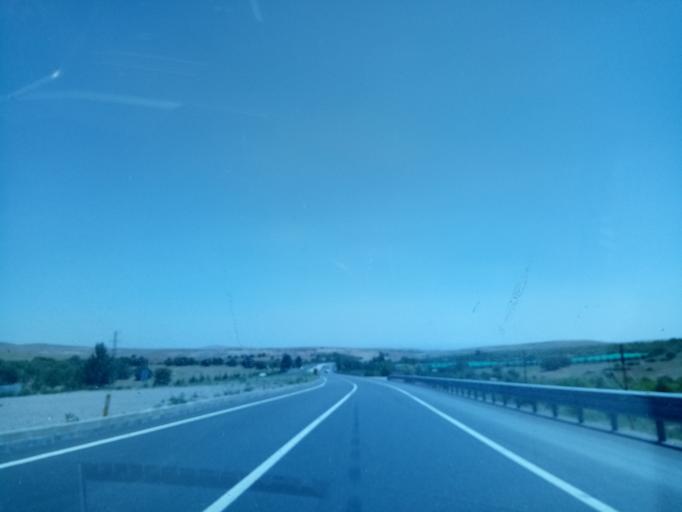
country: TR
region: Konya
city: Hatip
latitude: 37.7643
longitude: 32.2939
